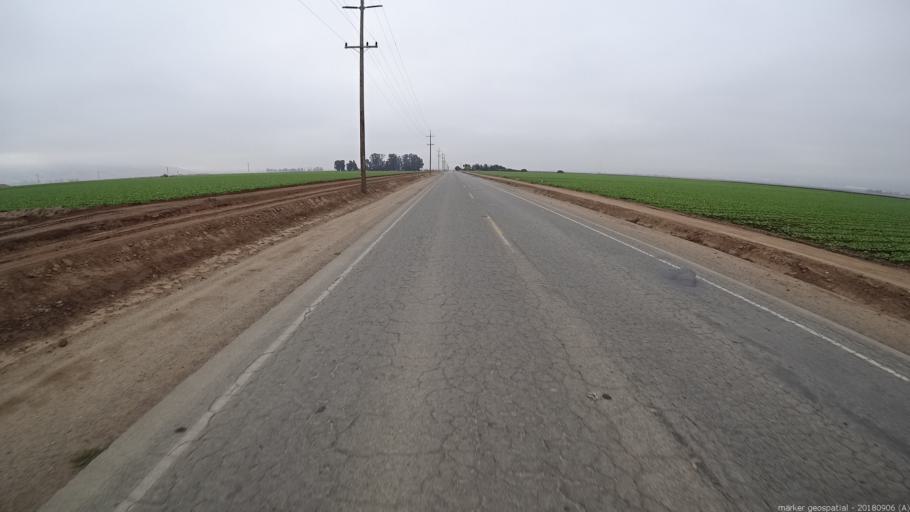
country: US
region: California
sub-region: Monterey County
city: Salinas
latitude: 36.6678
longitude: -121.5967
